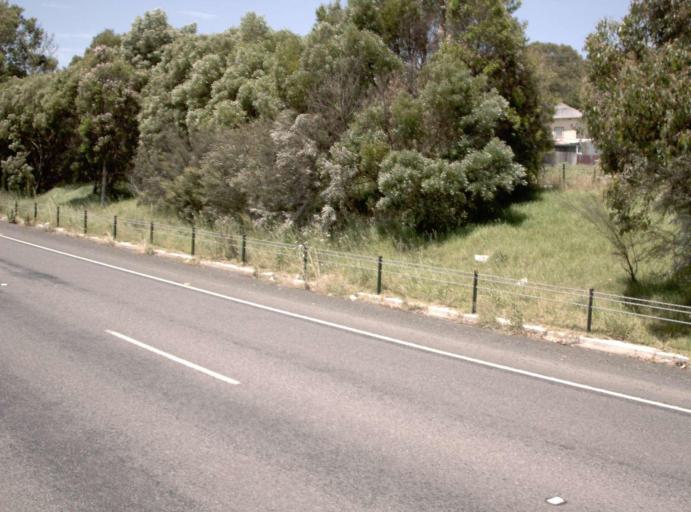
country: AU
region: Victoria
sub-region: Latrobe
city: Moe
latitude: -38.2000
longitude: 146.1938
